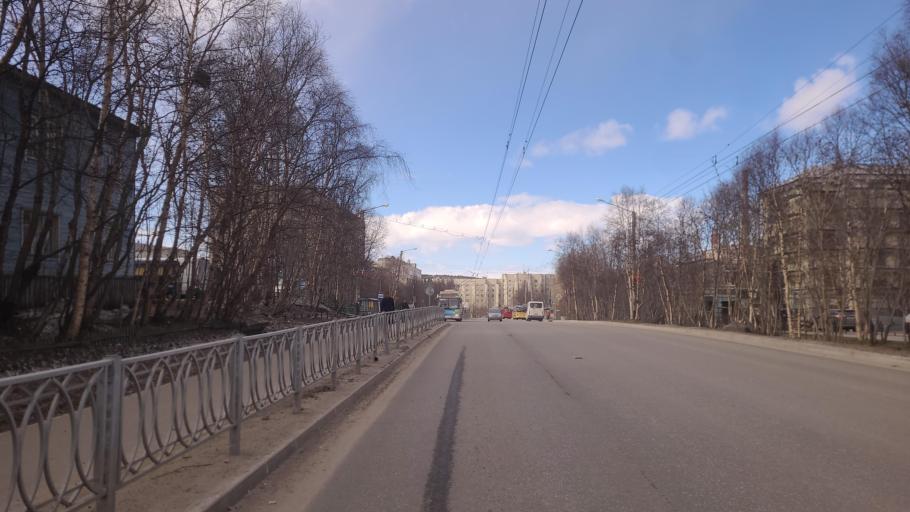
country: RU
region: Murmansk
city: Murmansk
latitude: 68.9532
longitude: 33.0686
